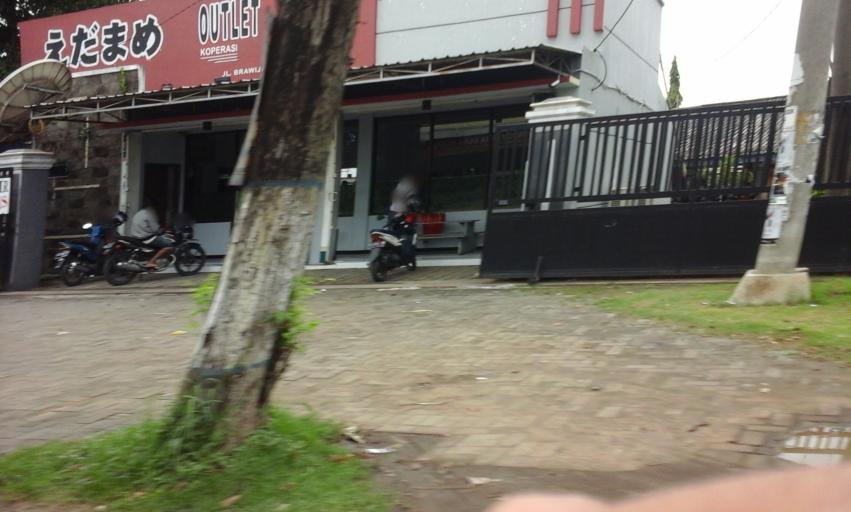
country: ID
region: East Java
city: Mangli
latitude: -8.1918
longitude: 113.6475
